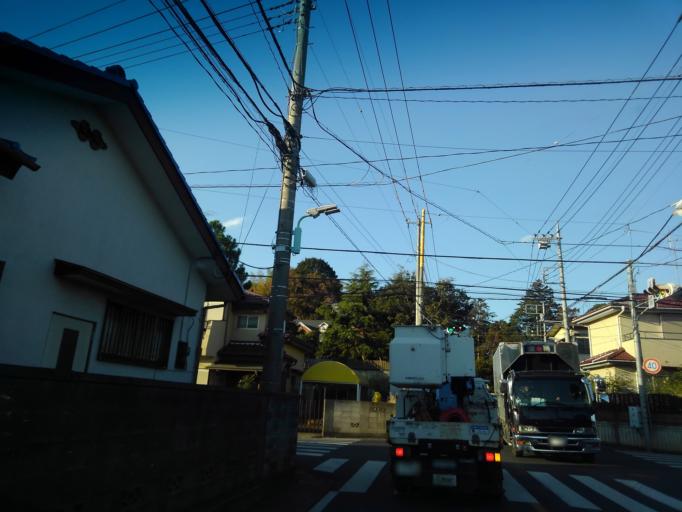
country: JP
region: Saitama
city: Tokorozawa
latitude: 35.7889
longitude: 139.4280
